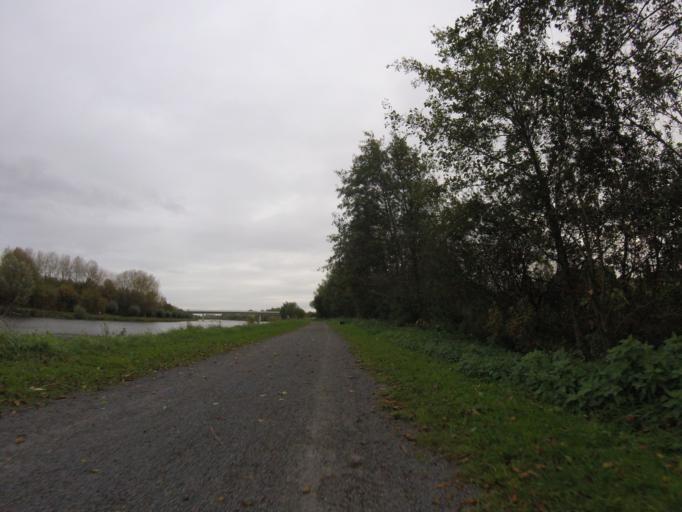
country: FR
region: Nord-Pas-de-Calais
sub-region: Departement du Nord
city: Quesnoy-sur-Deule
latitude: 50.6982
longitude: 3.0200
